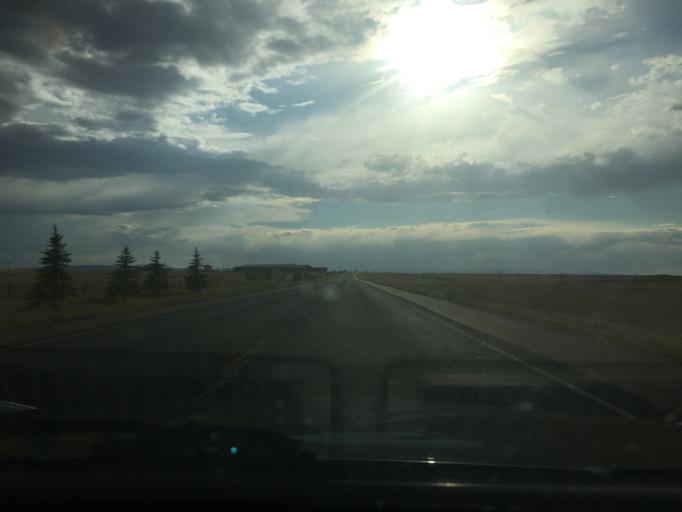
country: US
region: Wyoming
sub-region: Albany County
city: Laramie
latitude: 41.3199
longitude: -105.6454
